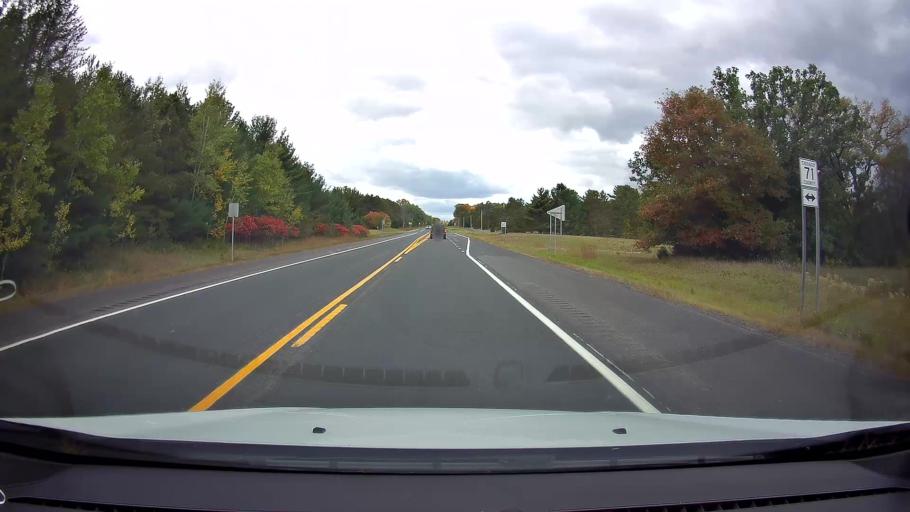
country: US
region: Wisconsin
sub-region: Polk County
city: Saint Croix Falls
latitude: 45.4190
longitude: -92.6599
